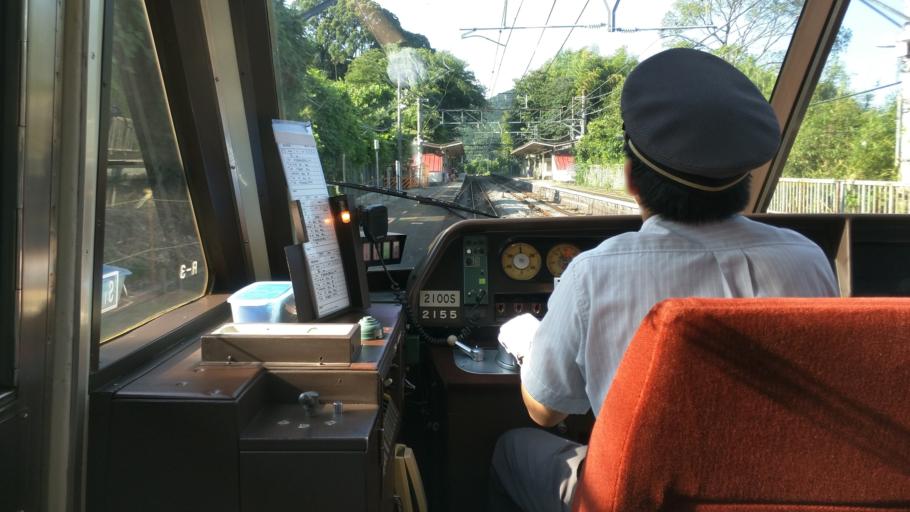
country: JP
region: Shizuoka
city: Atami
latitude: 35.0582
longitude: 139.0667
